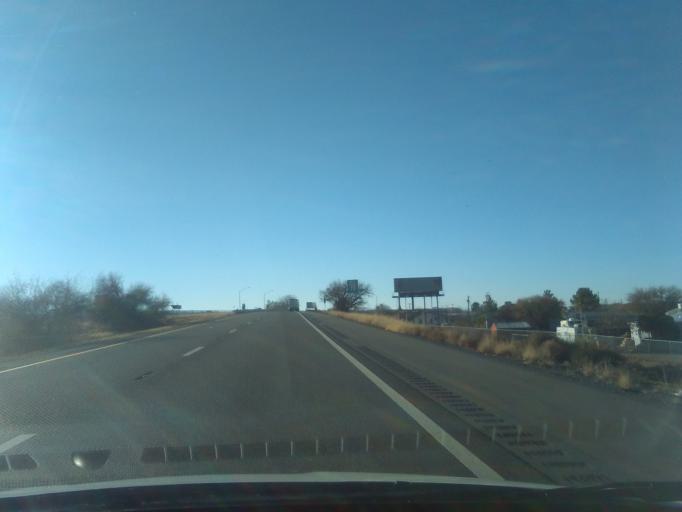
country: US
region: New Mexico
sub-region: Hidalgo County
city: Lordsburg
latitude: 32.3414
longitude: -108.7055
